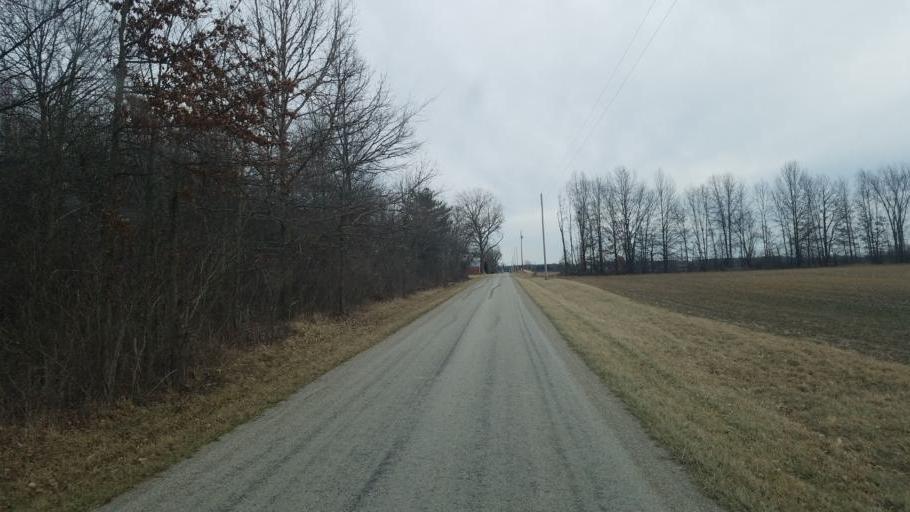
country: US
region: Ohio
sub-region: Morrow County
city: Cardington
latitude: 40.4780
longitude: -82.9214
